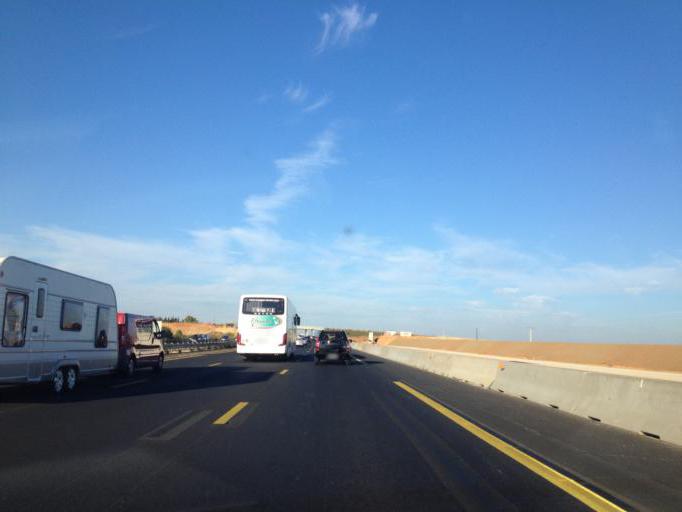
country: FR
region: Languedoc-Roussillon
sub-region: Departement de l'Herault
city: Saint-Aunes
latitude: 43.6280
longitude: 3.9650
